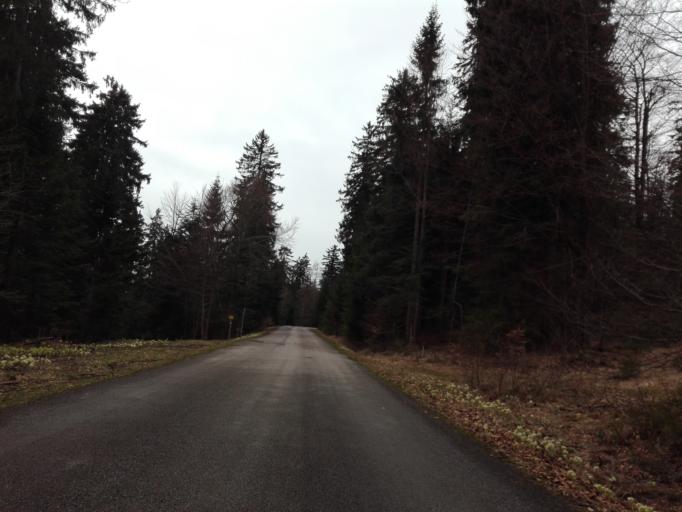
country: AT
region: Upper Austria
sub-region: Politischer Bezirk Rohrbach
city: Aigen im Muehlkreis
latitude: 48.6963
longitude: 13.9655
